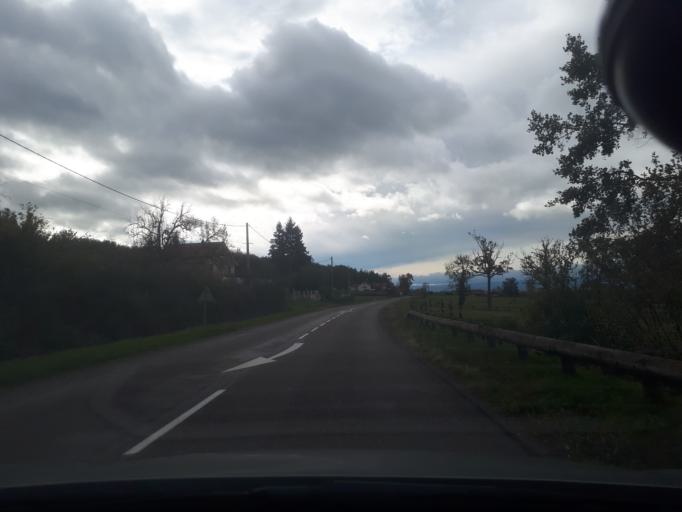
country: FR
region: Rhone-Alpes
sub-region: Departement de la Loire
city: Bellegarde-en-Forez
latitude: 45.6891
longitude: 4.3026
